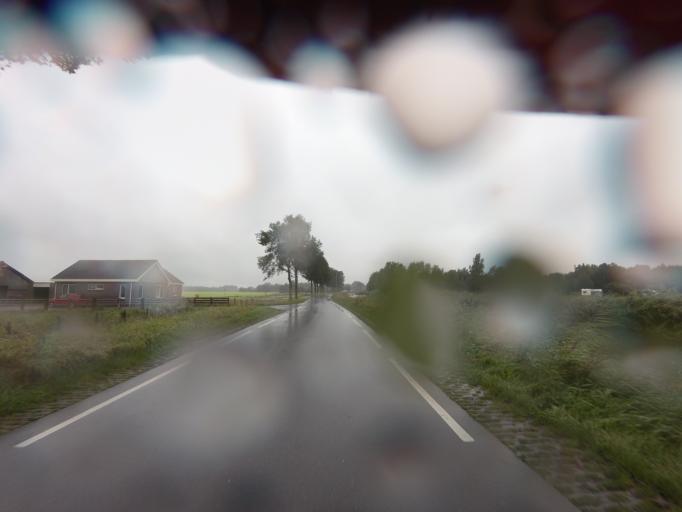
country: NL
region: North Holland
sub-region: Gemeente Medemblik
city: Opperdoes
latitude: 52.7283
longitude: 5.1019
